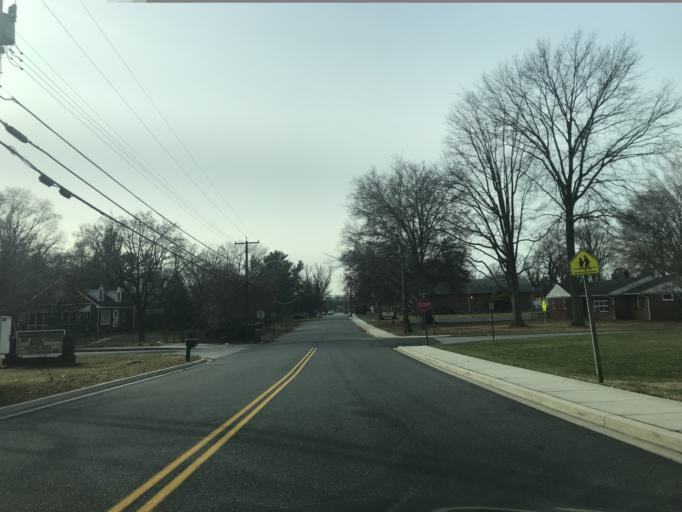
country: US
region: Maryland
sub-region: Harford County
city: Aberdeen
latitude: 39.5155
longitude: -76.1670
